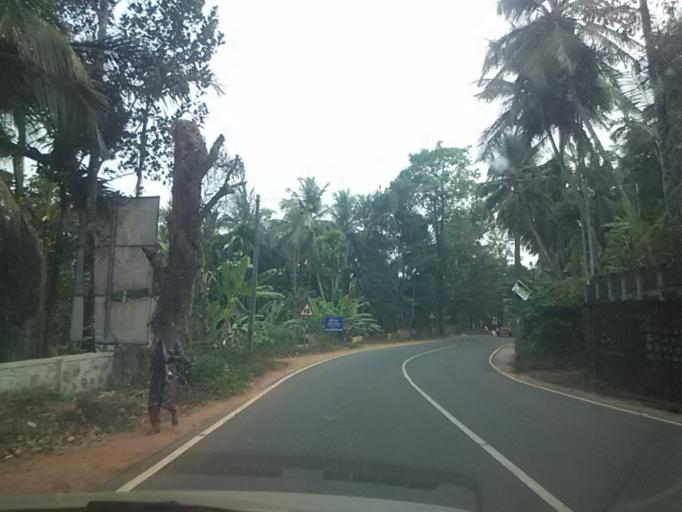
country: IN
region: Kerala
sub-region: Kozhikode
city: Naduvannur
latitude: 11.5102
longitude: 75.7754
